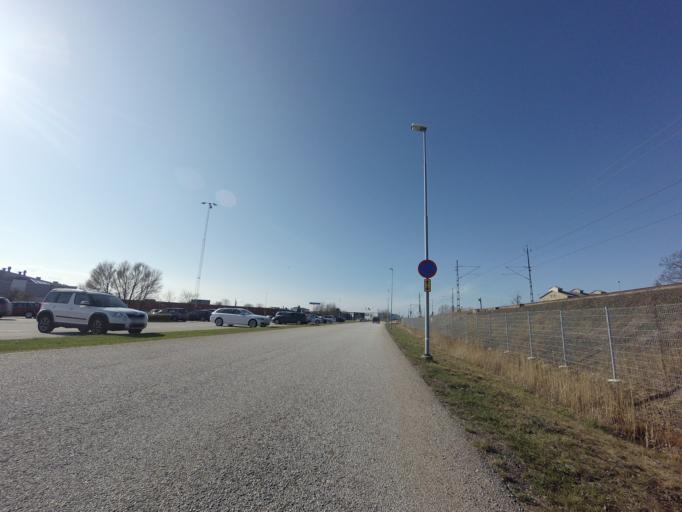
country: SE
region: Skane
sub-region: Landskrona
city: Landskrona
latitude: 55.8710
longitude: 12.8651
